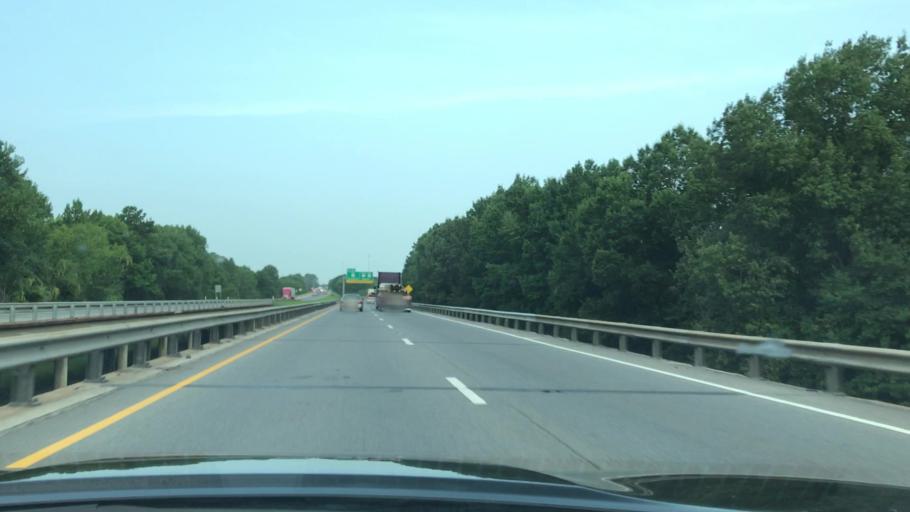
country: US
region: Texas
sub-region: Gregg County
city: Kilgore
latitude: 32.4351
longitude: -94.8154
